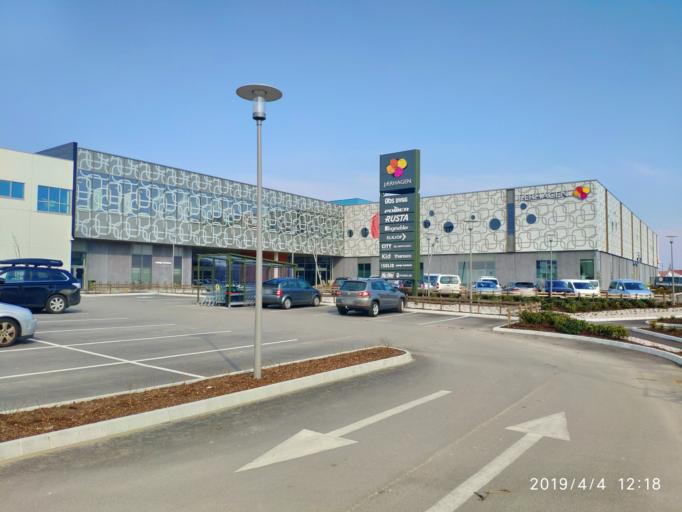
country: NO
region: Rogaland
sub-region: Klepp
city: Kleppe
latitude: 58.7791
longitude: 5.6283
